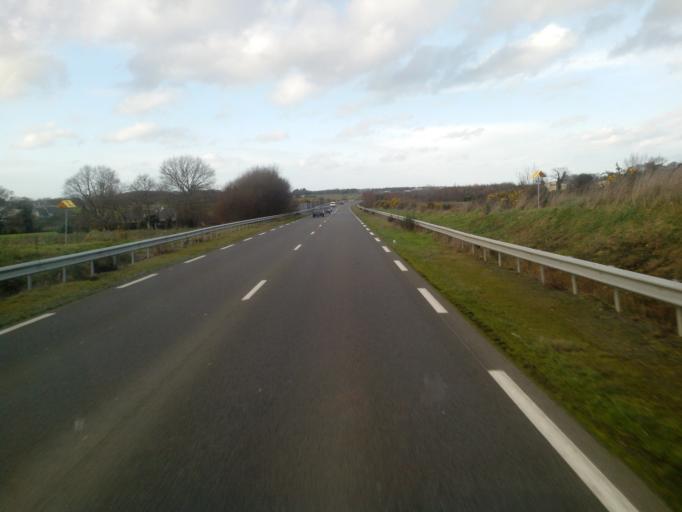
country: FR
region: Brittany
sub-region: Departement d'Ille-et-Vilaine
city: Pleurtuit
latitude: 48.5726
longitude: -2.0708
